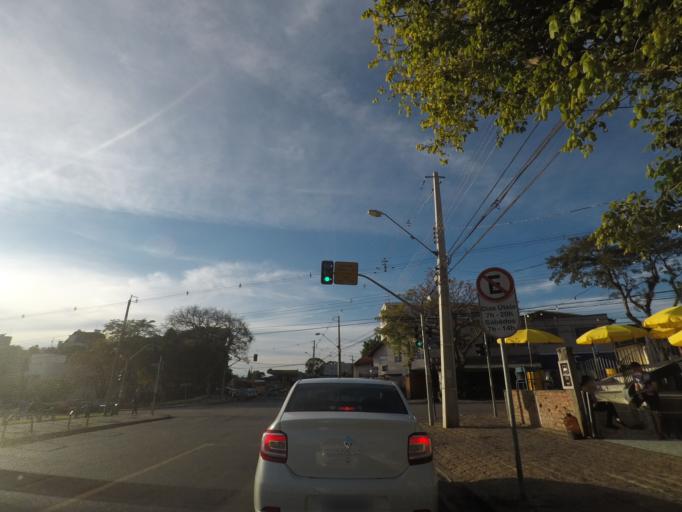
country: BR
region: Parana
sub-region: Curitiba
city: Curitiba
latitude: -25.4093
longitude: -49.2661
